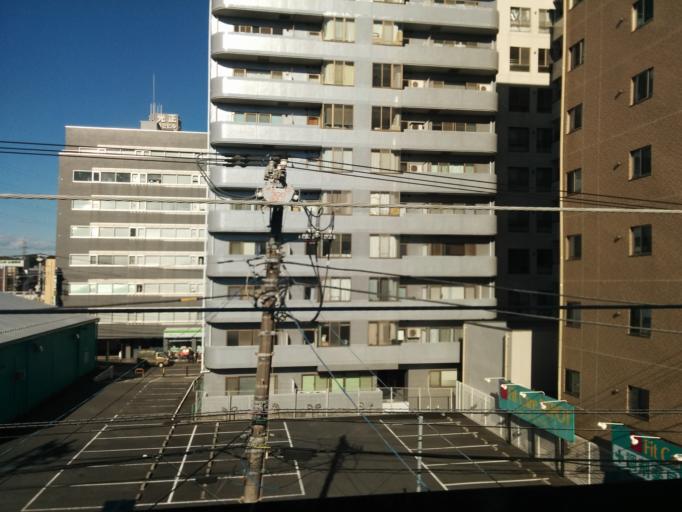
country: JP
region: Kanagawa
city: Yokohama
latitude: 35.5015
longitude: 139.6100
